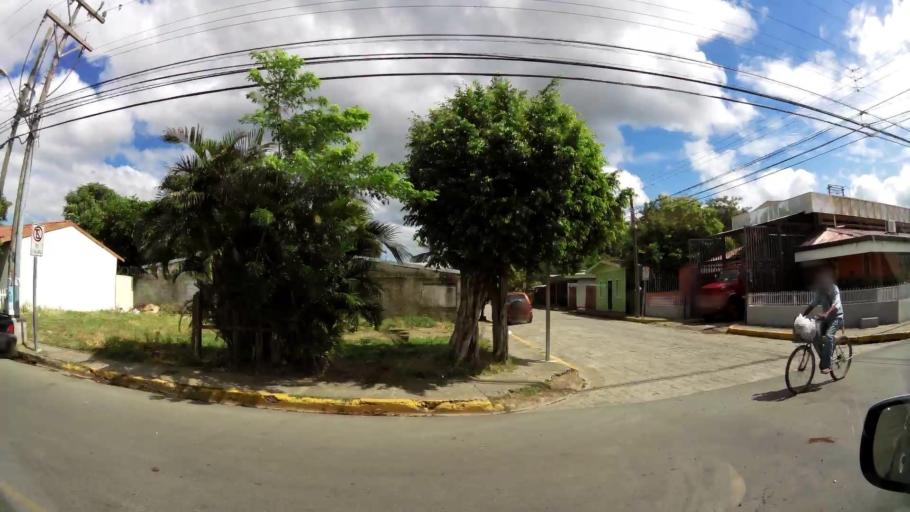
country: CR
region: Guanacaste
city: Santa Cruz
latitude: 10.2626
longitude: -85.5846
